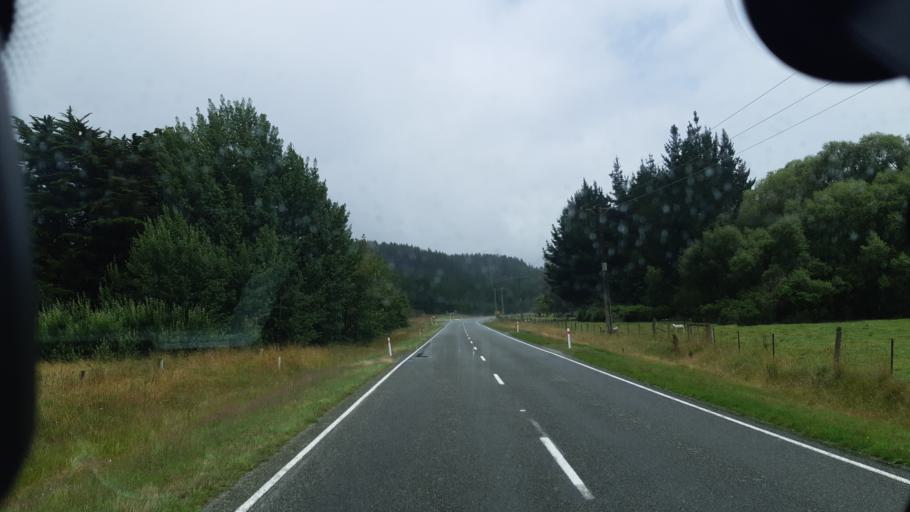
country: NZ
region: Canterbury
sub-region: Timaru District
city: Pleasant Point
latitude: -44.3095
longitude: 170.9486
